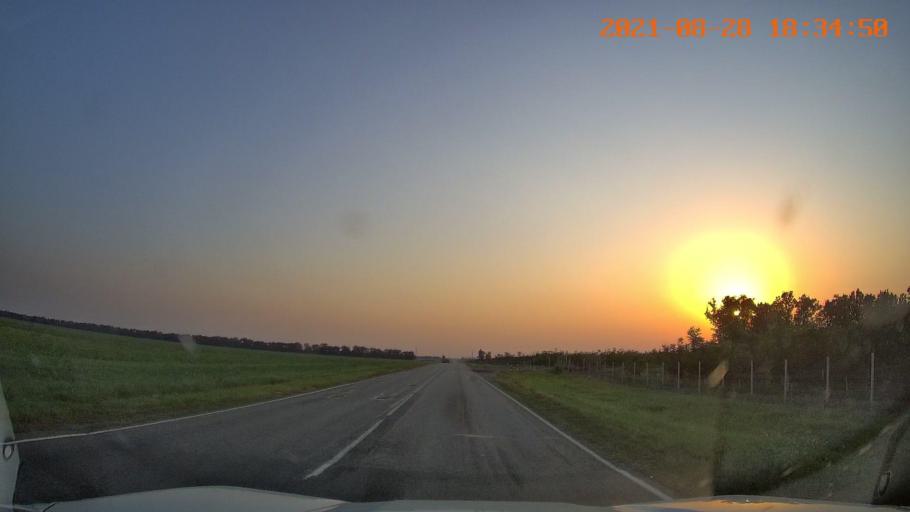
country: RU
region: Adygeya
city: Giaginskaya
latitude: 44.8767
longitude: 40.1465
